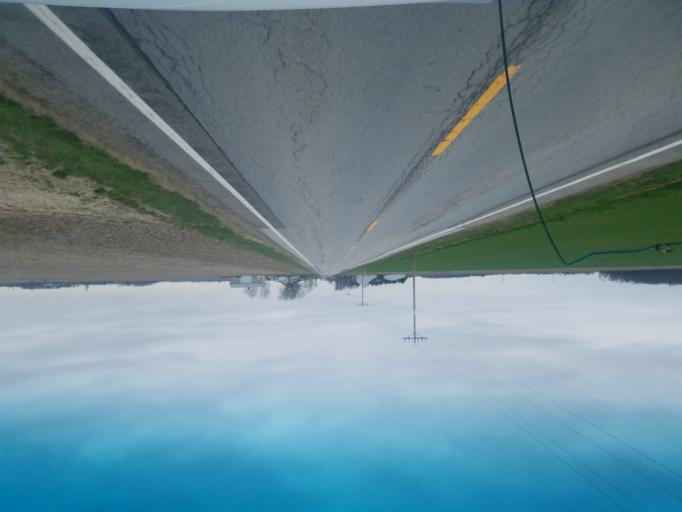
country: US
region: Ohio
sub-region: Allen County
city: Delphos
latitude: 40.9323
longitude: -84.3915
